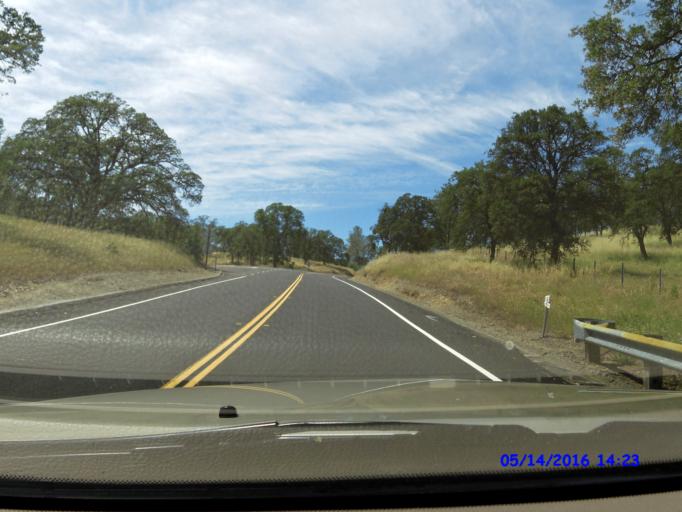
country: US
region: California
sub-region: Tuolumne County
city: Tuolumne City
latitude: 37.6932
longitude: -120.1812
